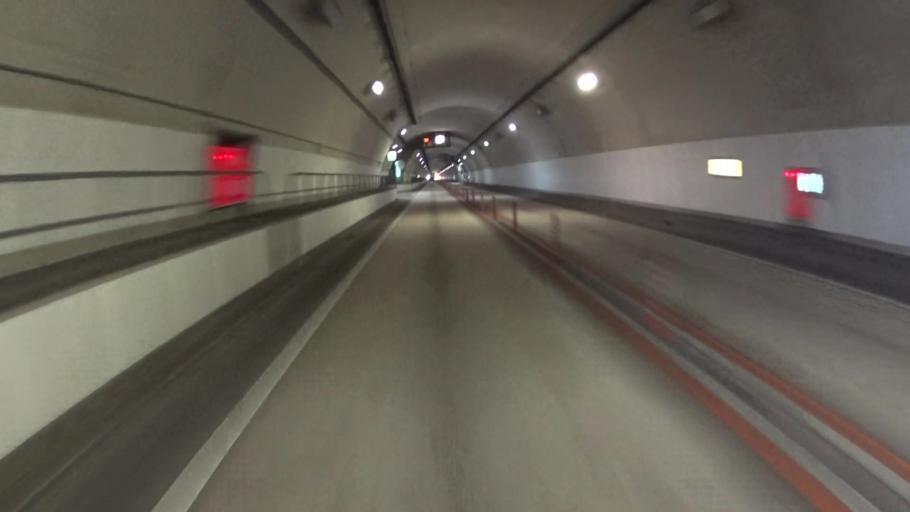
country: JP
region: Kyoto
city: Ayabe
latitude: 35.3251
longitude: 135.3149
